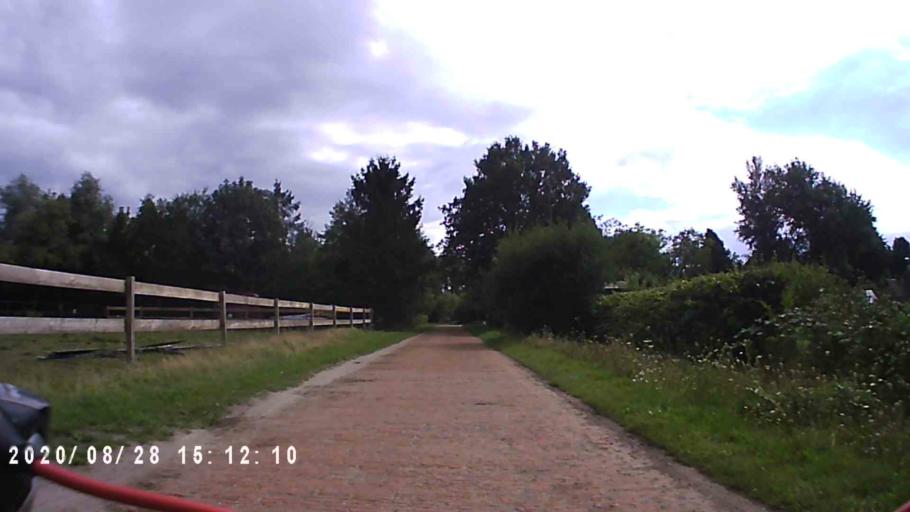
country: NL
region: Drenthe
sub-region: Gemeente Tynaarlo
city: Vries
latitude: 53.1267
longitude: 6.5749
